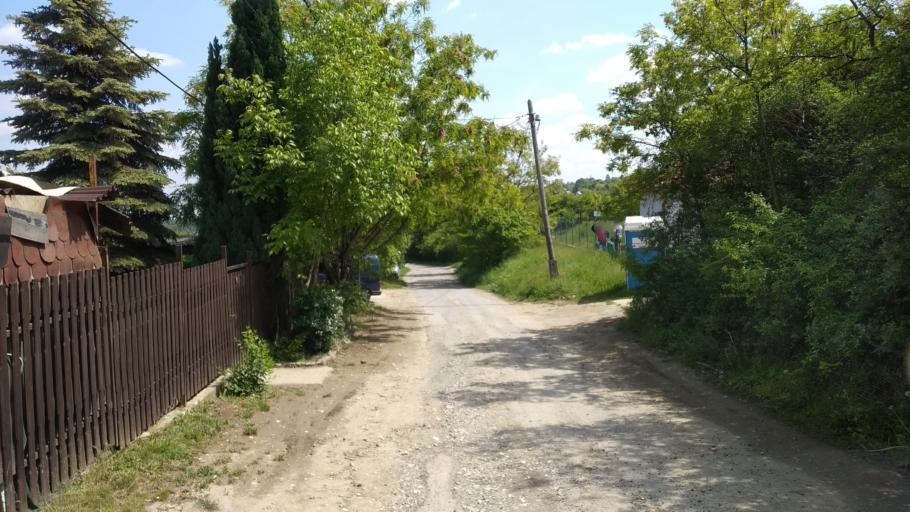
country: HU
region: Pest
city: Budakalasz
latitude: 47.6154
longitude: 19.0298
